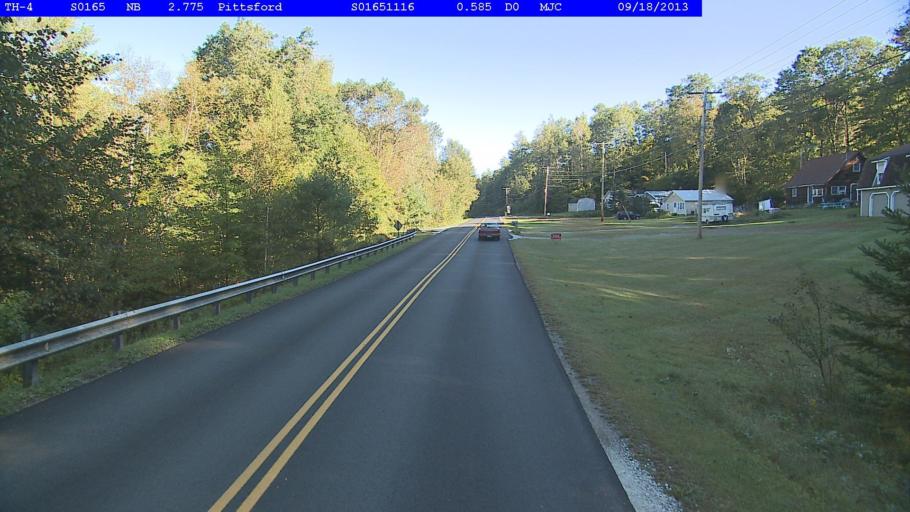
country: US
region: Vermont
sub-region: Rutland County
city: Rutland
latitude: 43.6778
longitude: -72.9457
